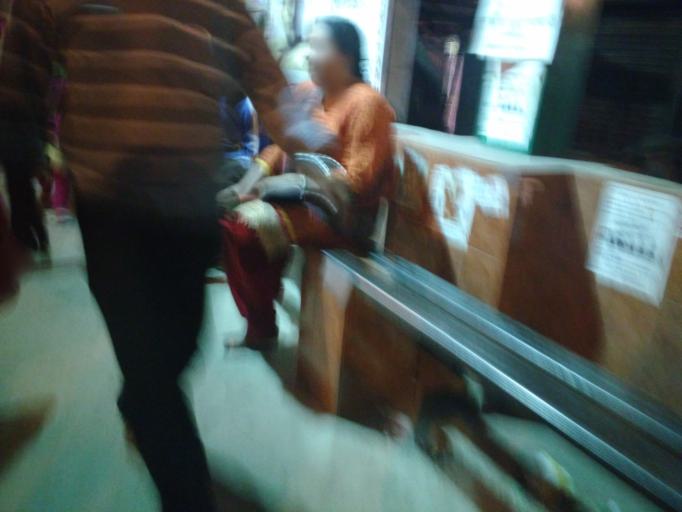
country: IN
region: West Bengal
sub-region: North 24 Parganas
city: Baranagar
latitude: 22.6313
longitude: 88.3785
